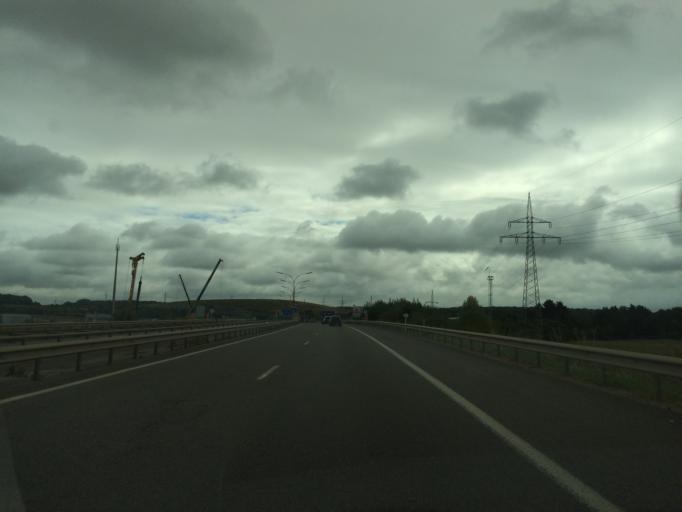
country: LU
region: Luxembourg
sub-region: Canton d'Esch-sur-Alzette
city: Bettembourg
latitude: 49.4966
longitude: 6.1044
